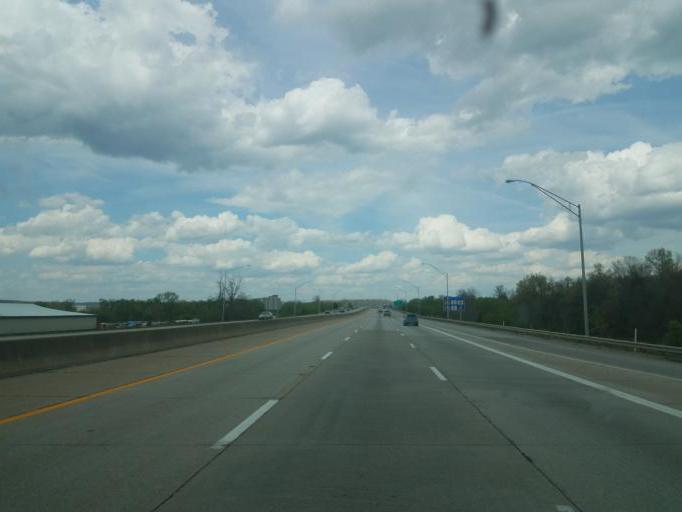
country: US
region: Kentucky
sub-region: Bullitt County
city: Shepherdsville
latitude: 37.9809
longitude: -85.6989
